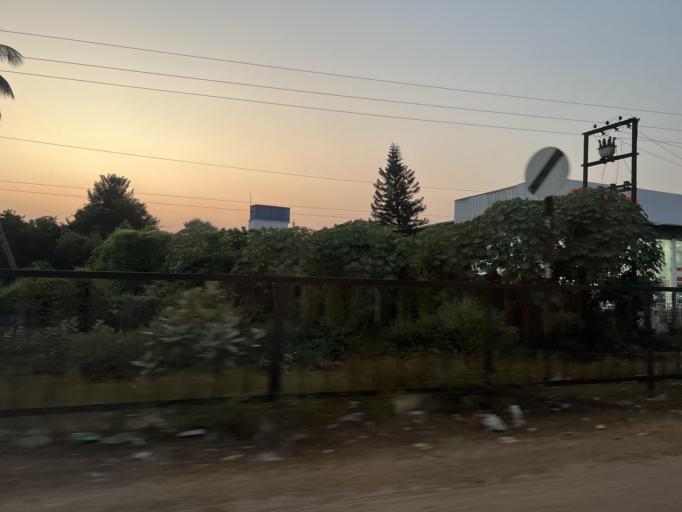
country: IN
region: Odisha
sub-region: Cuttack
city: Cuttack
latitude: 20.3949
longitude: 85.8824
